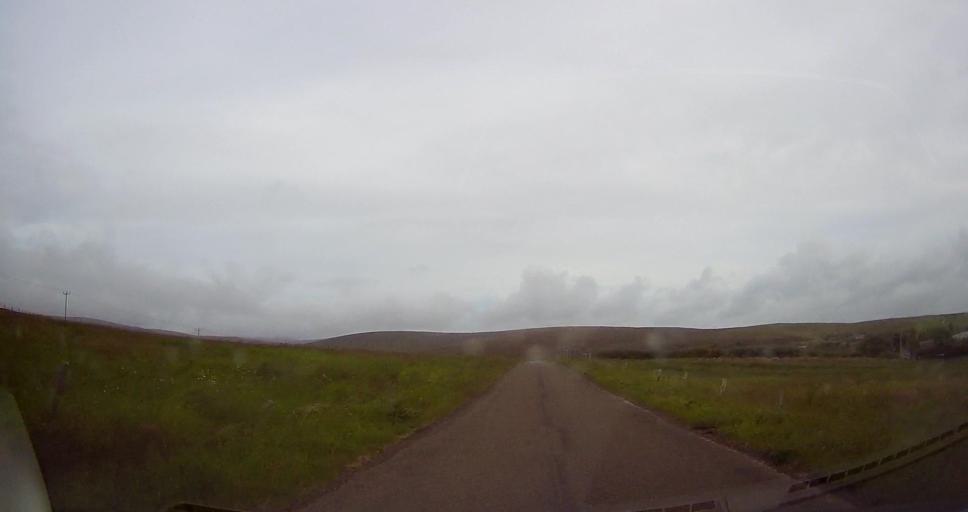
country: GB
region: Scotland
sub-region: Orkney Islands
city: Stromness
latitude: 58.8362
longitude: -3.2145
